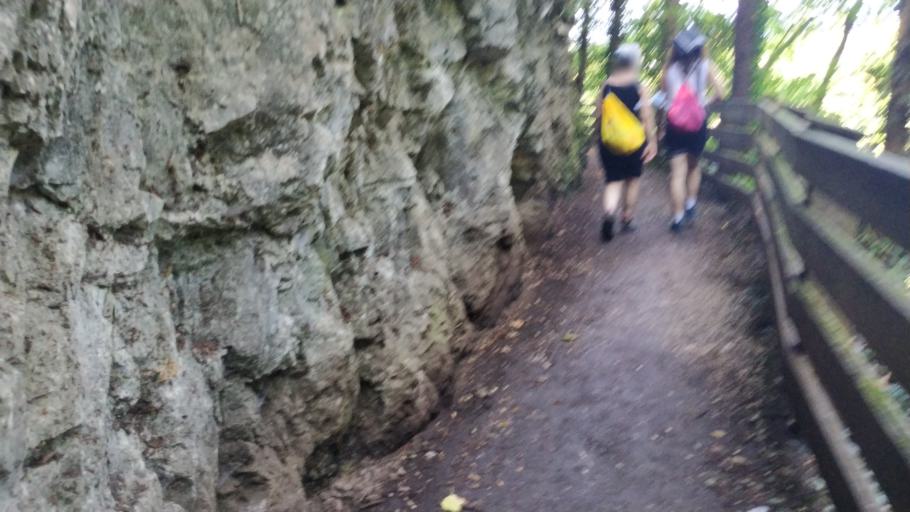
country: IT
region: Trentino-Alto Adige
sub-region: Provincia di Trento
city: Sanzeno
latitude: 46.3697
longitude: 11.0853
